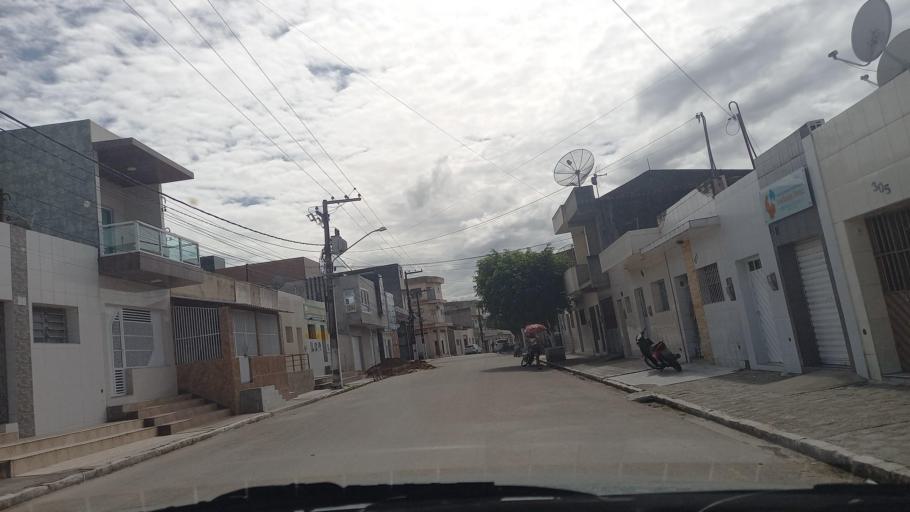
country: BR
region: Pernambuco
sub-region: Cachoeirinha
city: Cachoeirinha
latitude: -8.4901
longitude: -36.2335
